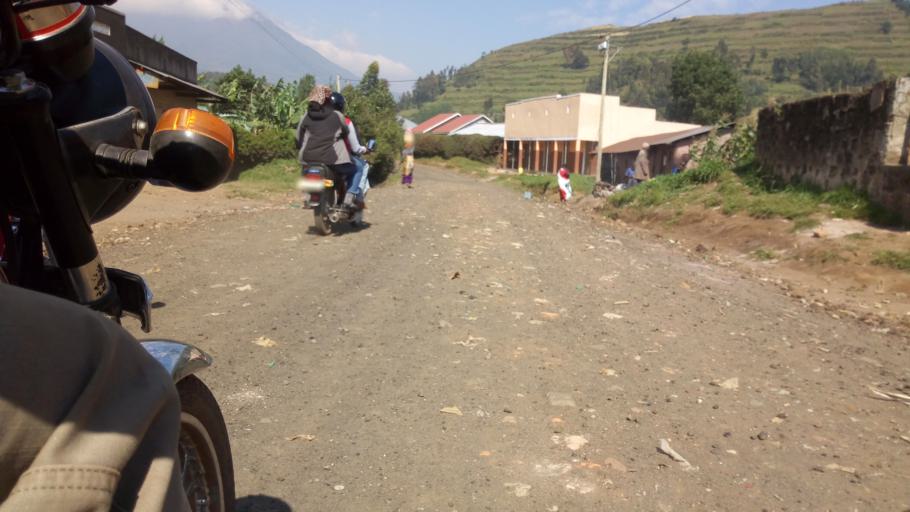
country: UG
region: Western Region
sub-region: Kisoro District
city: Kisoro
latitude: -1.3328
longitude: 29.6379
